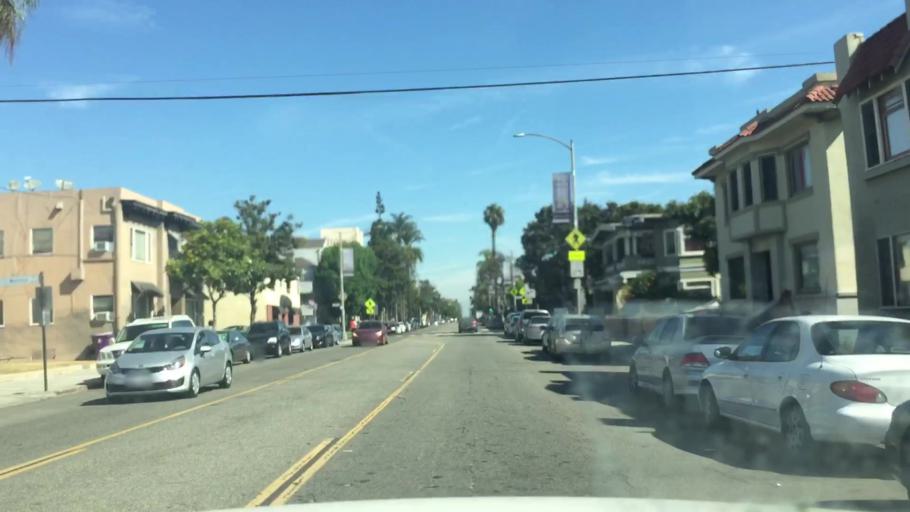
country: US
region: California
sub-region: Los Angeles County
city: Long Beach
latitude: 33.7720
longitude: -118.1980
